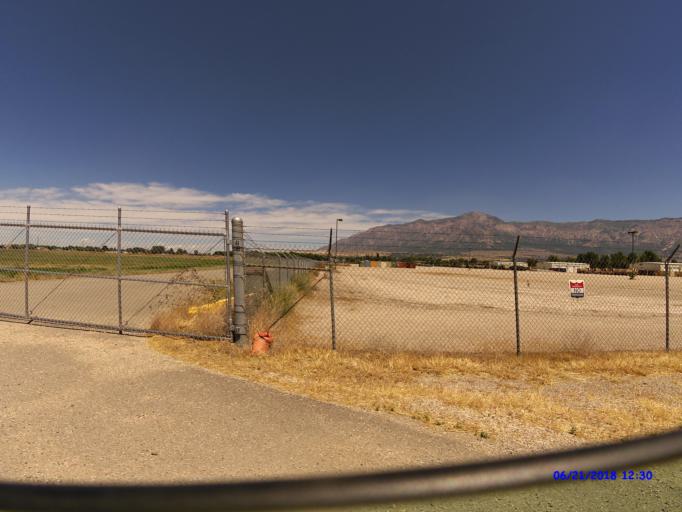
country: US
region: Utah
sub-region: Weber County
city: Harrisville
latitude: 41.2762
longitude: -112.0027
